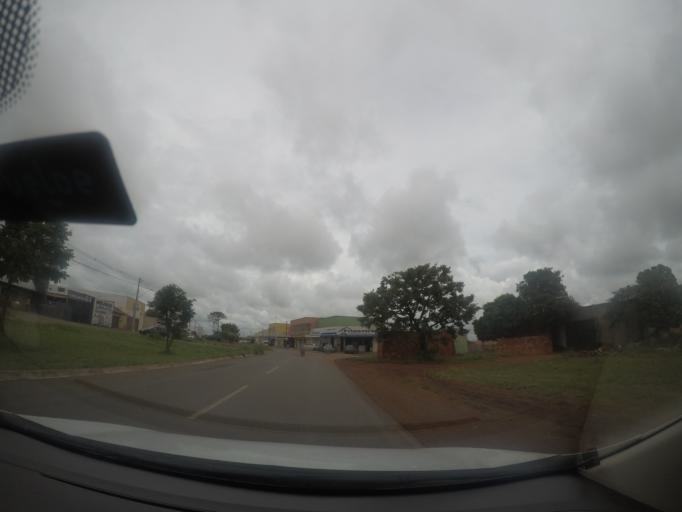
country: BR
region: Goias
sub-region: Trindade
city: Trindade
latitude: -16.6841
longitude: -49.3929
